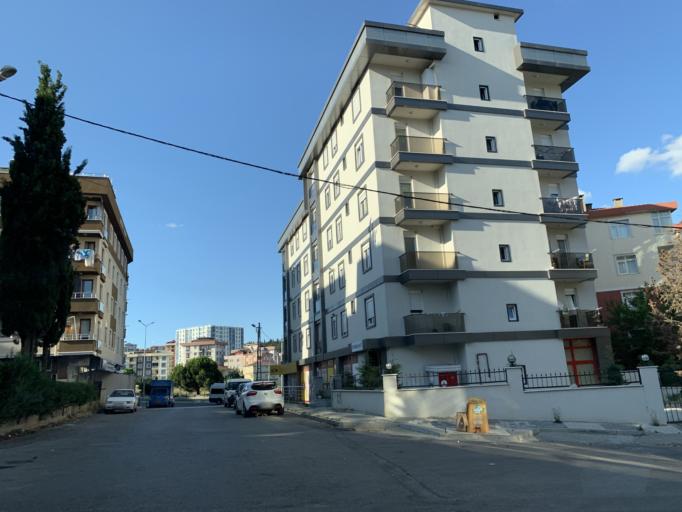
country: TR
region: Istanbul
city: Pendik
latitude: 40.8951
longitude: 29.2570
